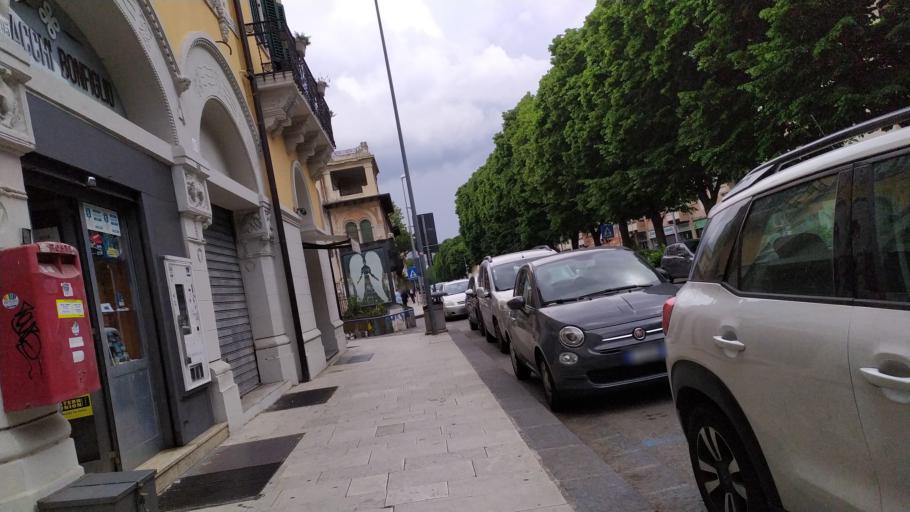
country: IT
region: Sicily
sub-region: Messina
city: Messina
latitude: 38.1909
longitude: 15.5565
